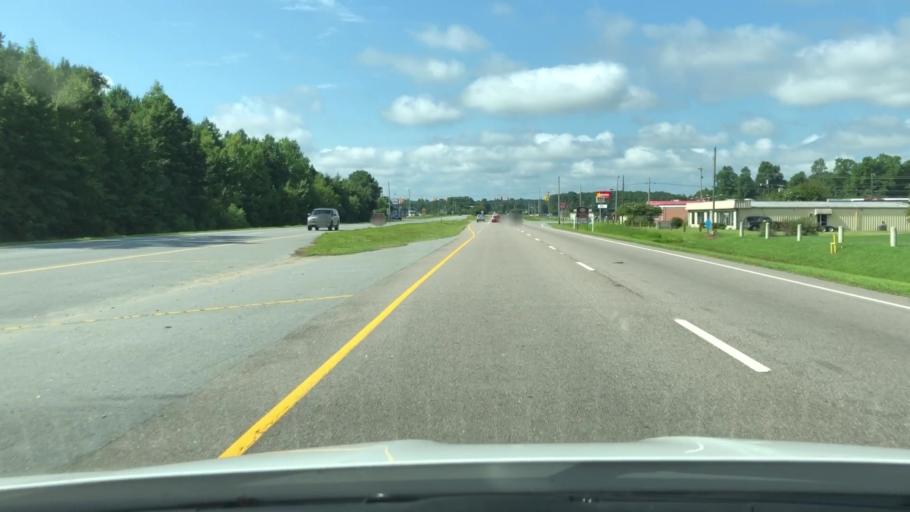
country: US
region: North Carolina
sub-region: Perquimans County
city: Hertford
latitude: 36.1802
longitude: -76.4607
